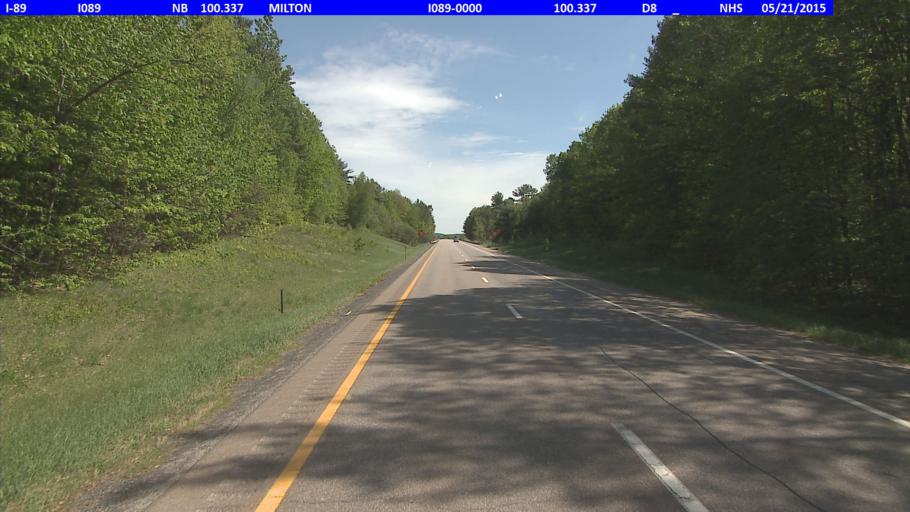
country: US
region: Vermont
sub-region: Chittenden County
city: Milton
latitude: 44.6220
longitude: -73.1555
